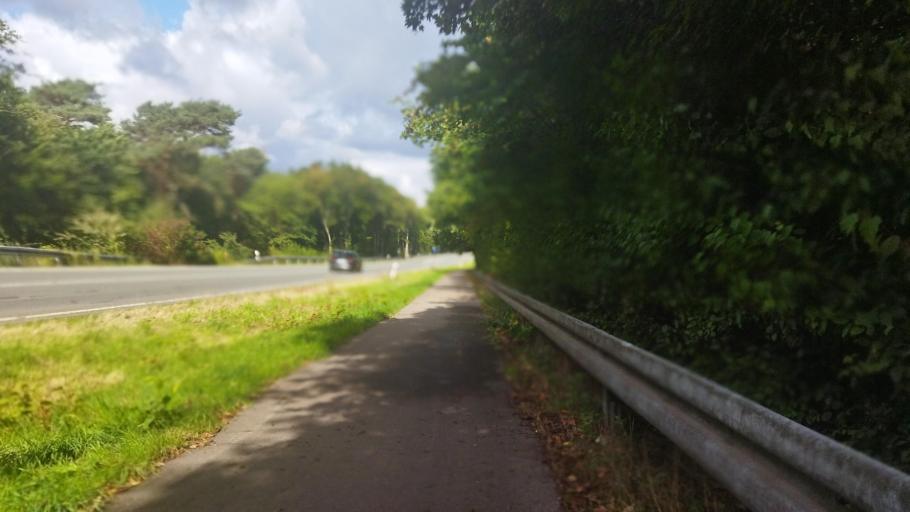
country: DE
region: North Rhine-Westphalia
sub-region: Regierungsbezirk Munster
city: Haltern
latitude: 51.6986
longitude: 7.1901
